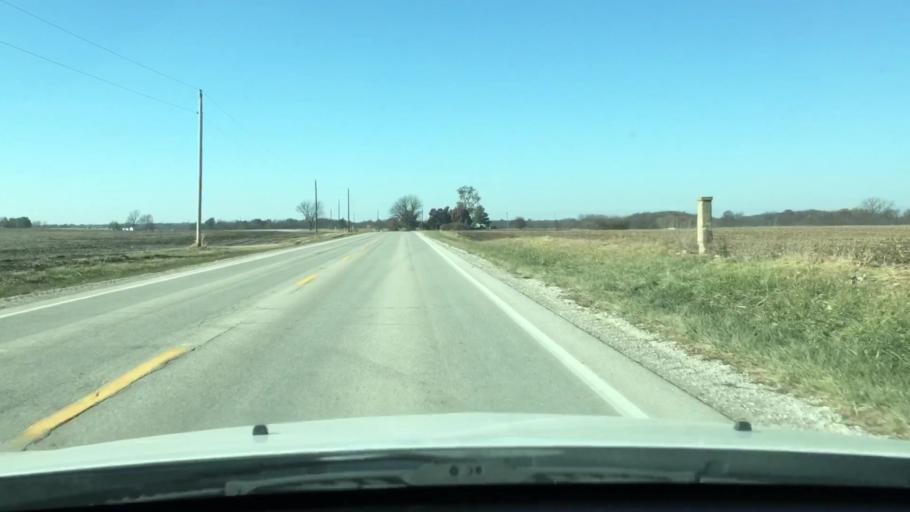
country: US
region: Illinois
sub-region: Pike County
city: Pittsfield
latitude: 39.6195
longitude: -90.7180
